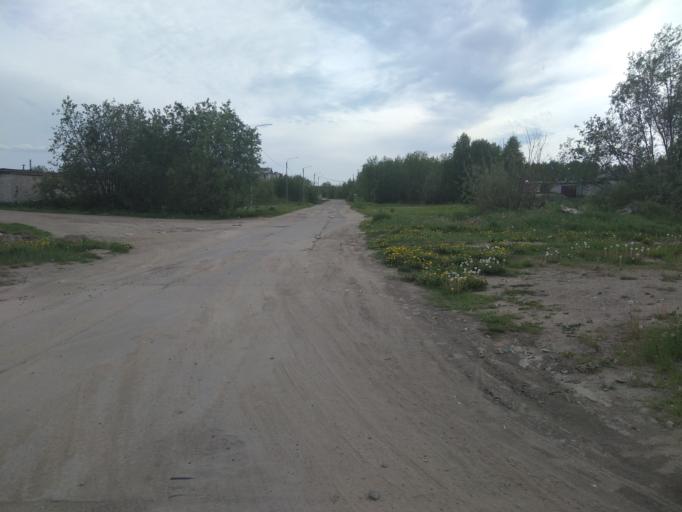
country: RU
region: Komi Republic
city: Pechora
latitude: 65.1428
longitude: 57.2474
